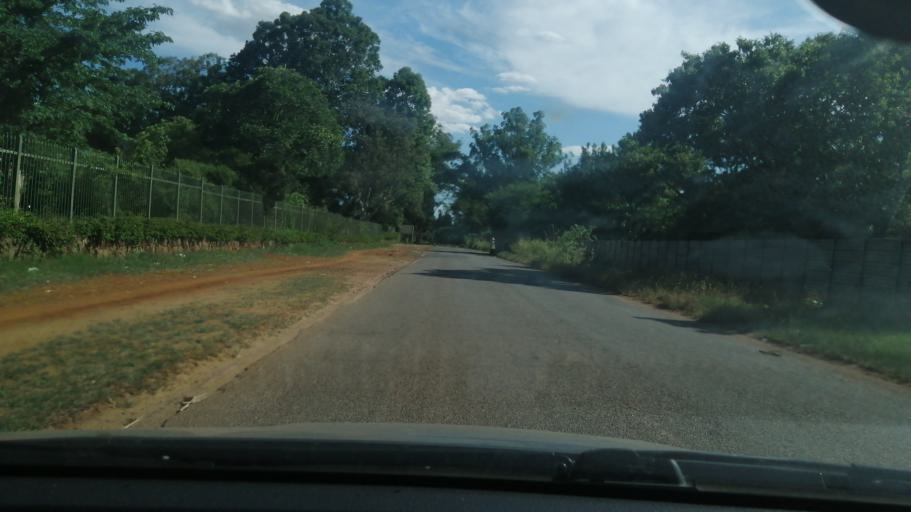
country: ZW
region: Harare
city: Harare
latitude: -17.8006
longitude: 31.0508
